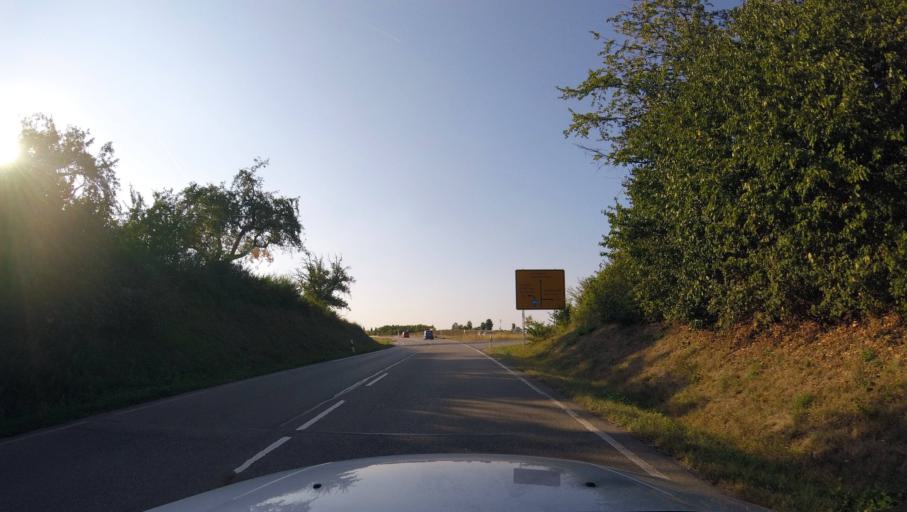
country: DE
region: Baden-Wuerttemberg
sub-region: Regierungsbezirk Stuttgart
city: Leutenbach
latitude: 48.8994
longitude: 9.4217
